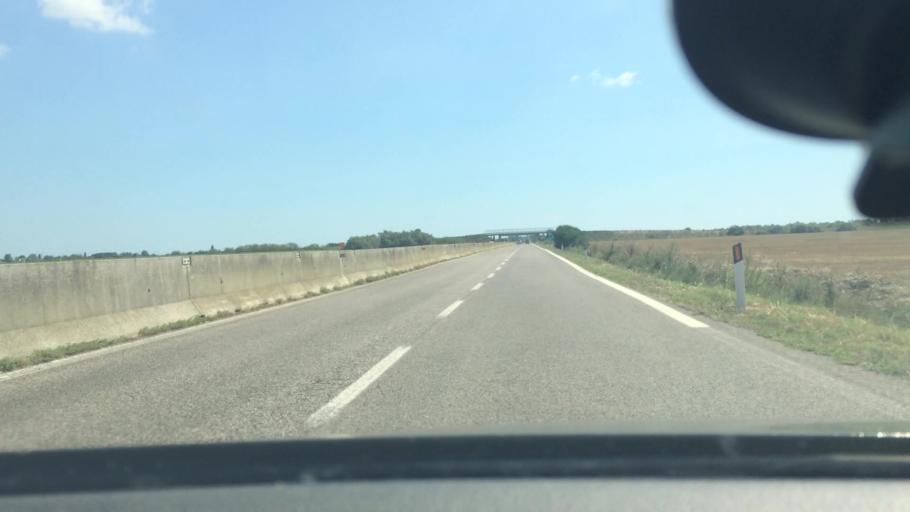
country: IT
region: Emilia-Romagna
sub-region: Provincia di Ferrara
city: Ostellato
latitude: 44.7550
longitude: 11.9767
